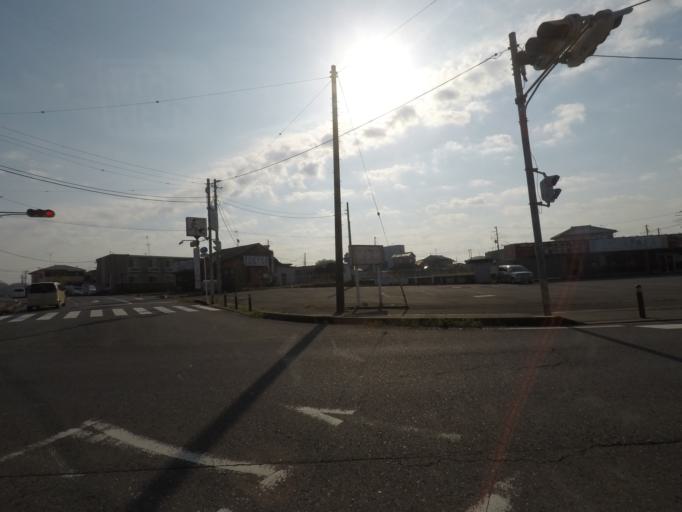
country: JP
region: Chiba
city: Narita
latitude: 35.7329
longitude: 140.3157
